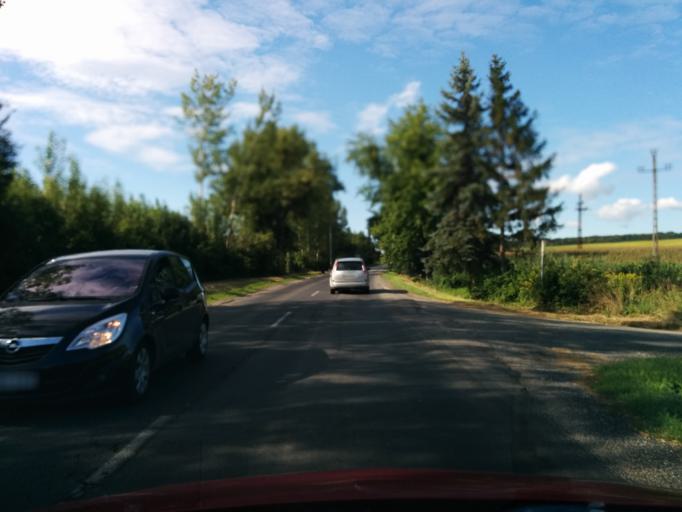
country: AT
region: Burgenland
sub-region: Politischer Bezirk Oberpullendorf
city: Lutzmannsburg
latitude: 47.4098
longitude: 16.6218
